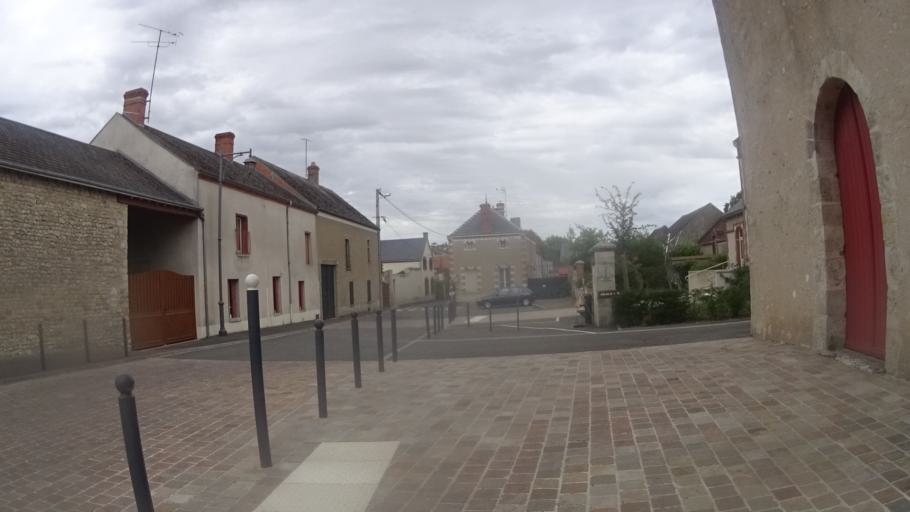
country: FR
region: Centre
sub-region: Departement du Loiret
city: Boynes
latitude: 48.0975
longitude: 2.3164
